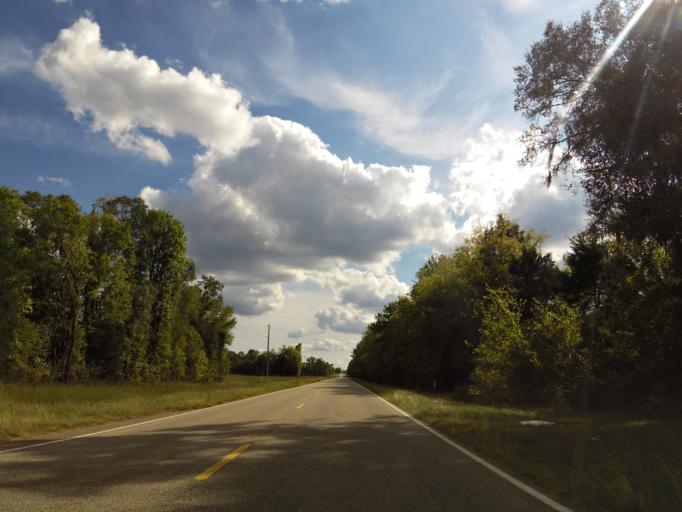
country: US
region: Alabama
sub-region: Dallas County
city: Selmont-West Selmont
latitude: 32.2389
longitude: -86.9940
